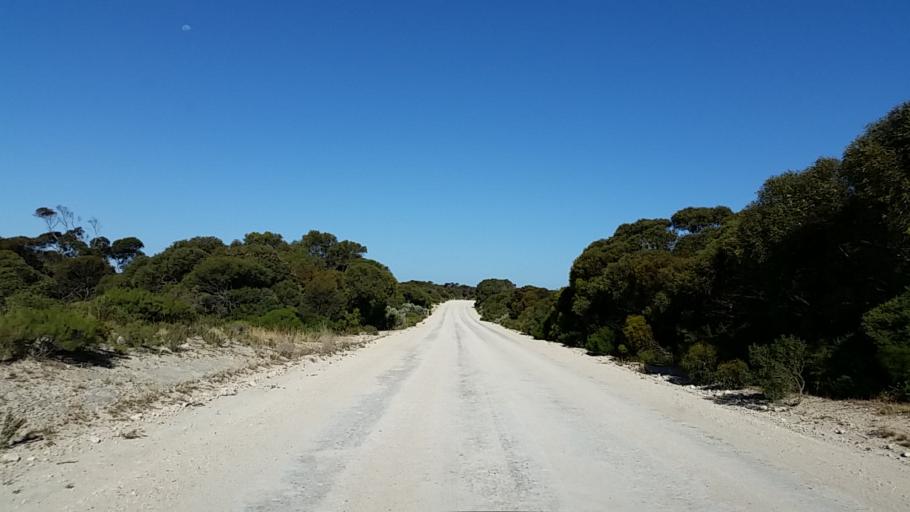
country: AU
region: South Australia
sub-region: Yorke Peninsula
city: Honiton
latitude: -35.2292
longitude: 137.1160
